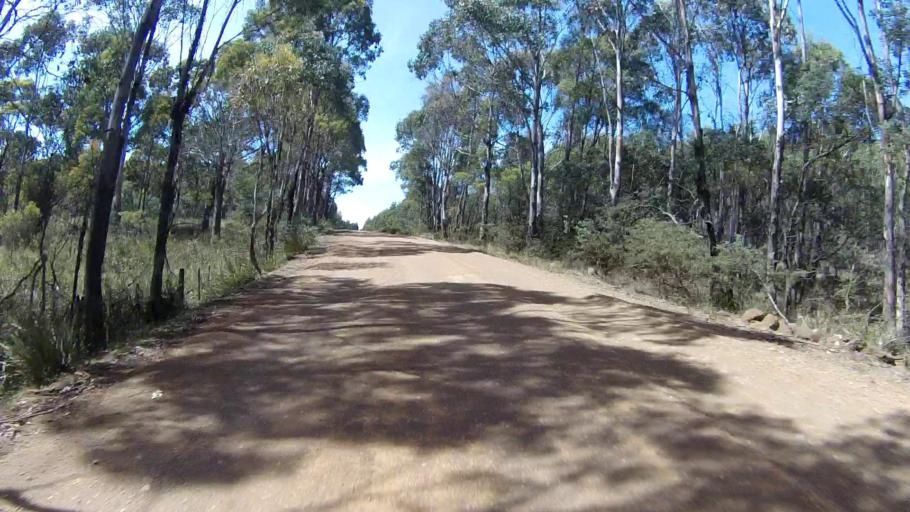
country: AU
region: Tasmania
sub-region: Sorell
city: Sorell
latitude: -42.6867
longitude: 147.7323
